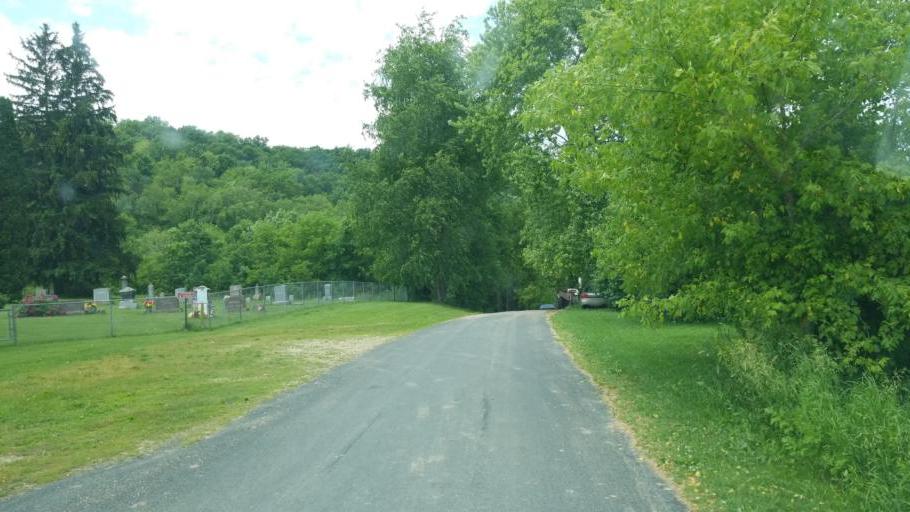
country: US
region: Wisconsin
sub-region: Monroe County
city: Cashton
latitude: 43.7264
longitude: -90.6669
